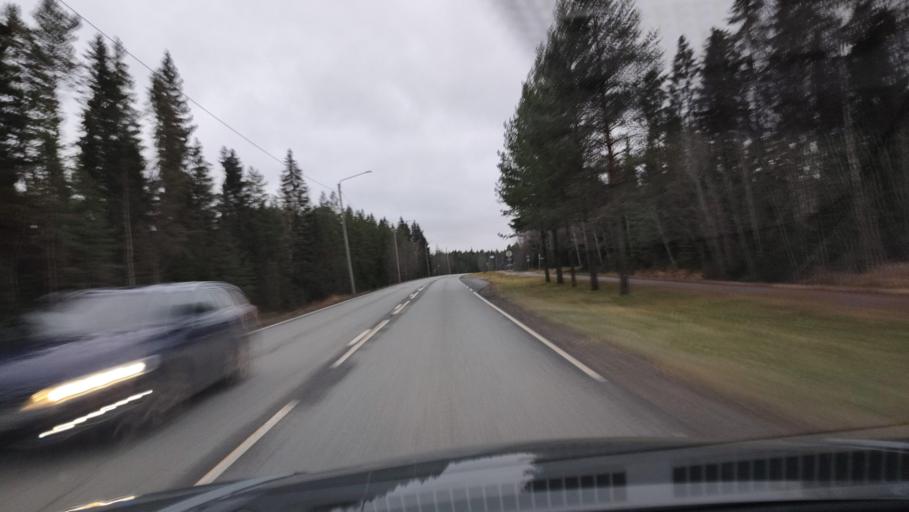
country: FI
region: Southern Ostrobothnia
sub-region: Suupohja
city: Kauhajoki
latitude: 62.3981
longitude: 22.1579
